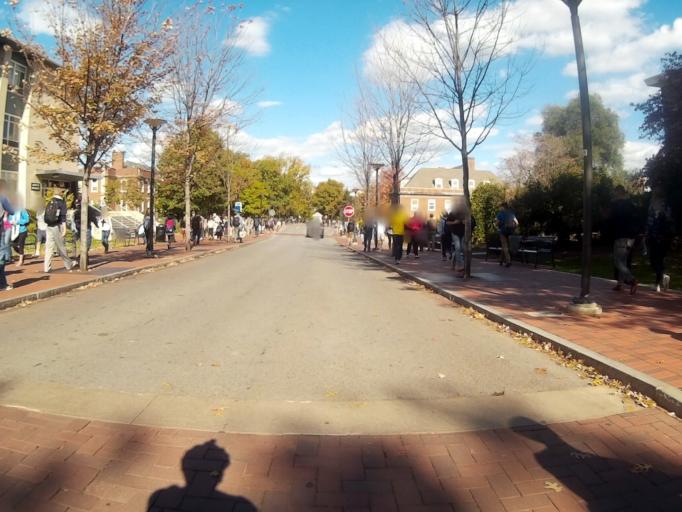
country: US
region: Pennsylvania
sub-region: Centre County
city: State College
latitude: 40.7987
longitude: -77.8614
